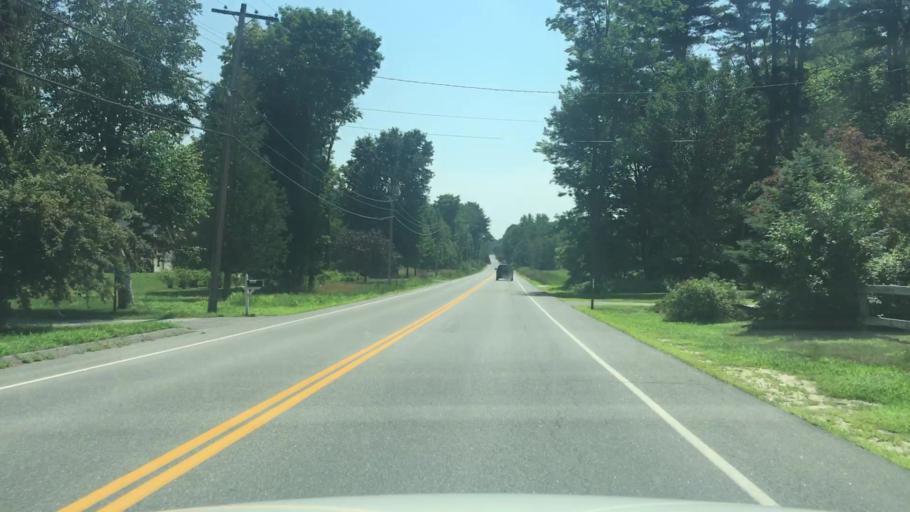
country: US
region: Maine
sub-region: Cumberland County
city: Cumberland Center
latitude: 43.8090
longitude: -70.2835
